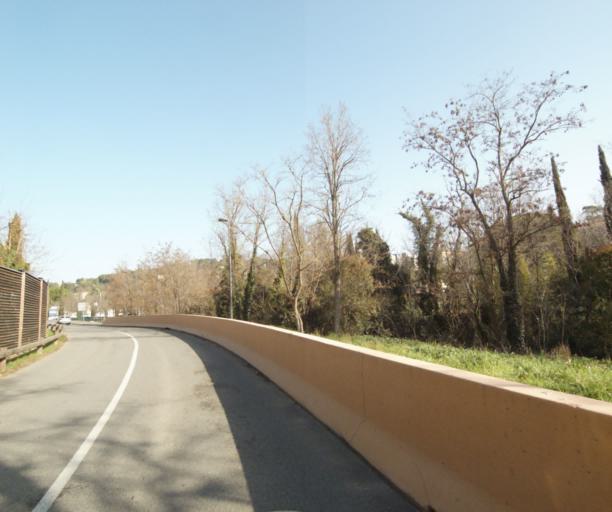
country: FR
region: Provence-Alpes-Cote d'Azur
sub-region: Departement des Bouches-du-Rhone
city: Aix-en-Provence
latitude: 43.5324
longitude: 5.4602
